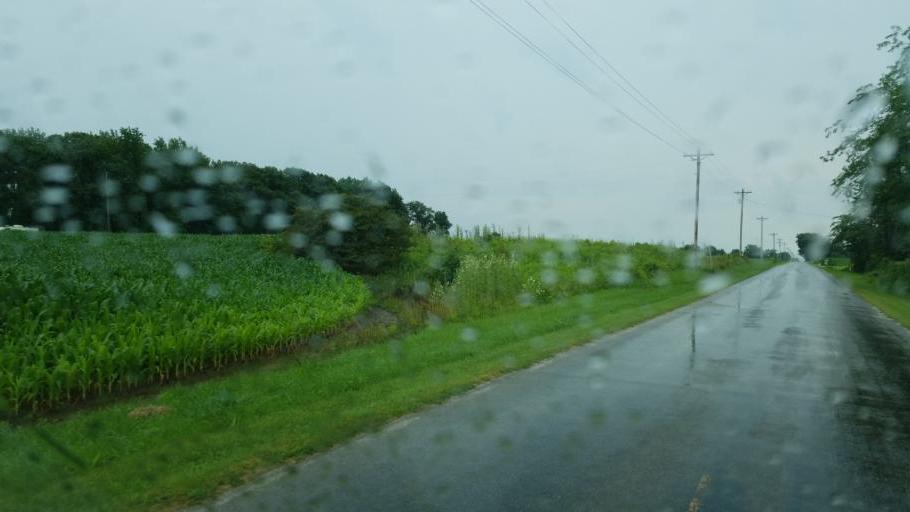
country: US
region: Ohio
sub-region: Union County
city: Richwood
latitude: 40.5403
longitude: -83.4372
